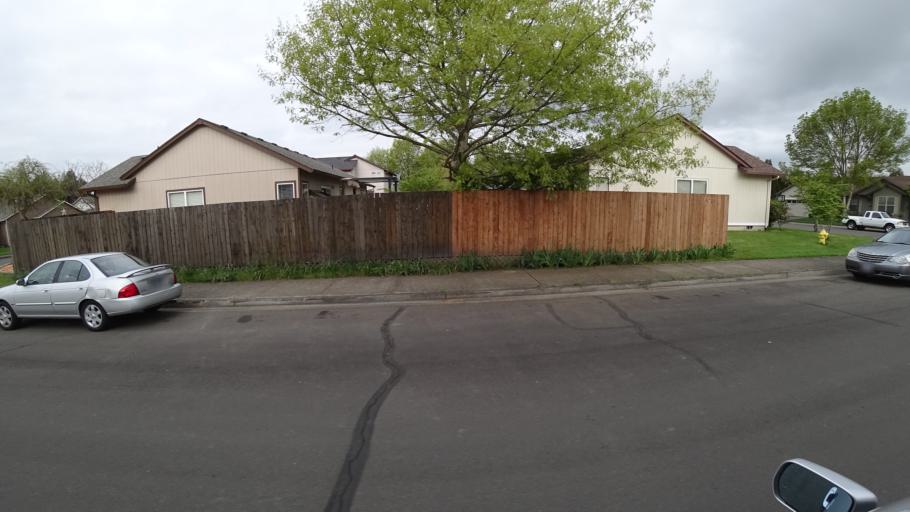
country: US
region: Oregon
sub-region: Washington County
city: Hillsboro
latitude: 45.5336
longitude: -122.9593
